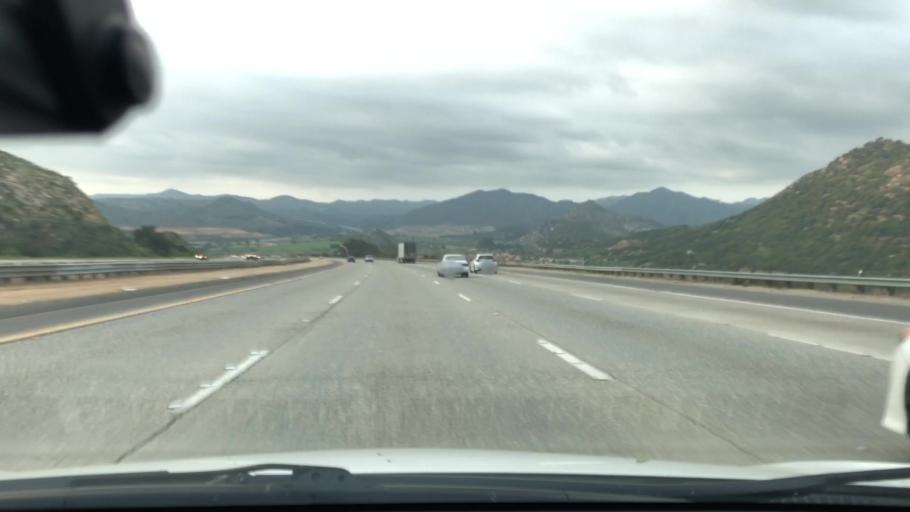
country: US
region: California
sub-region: San Diego County
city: Bonsall
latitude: 33.3073
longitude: -117.1503
